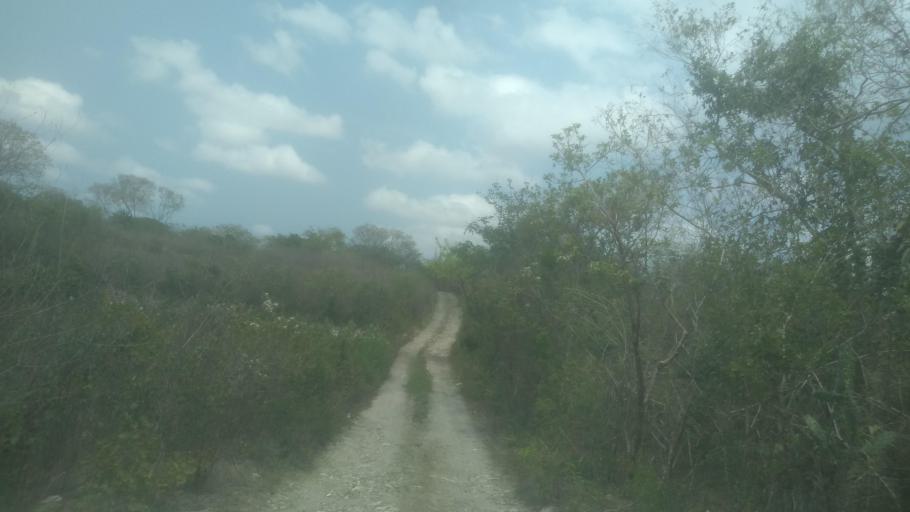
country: MX
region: Veracruz
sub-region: Emiliano Zapata
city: Plan del Rio
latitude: 19.3871
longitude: -96.6348
